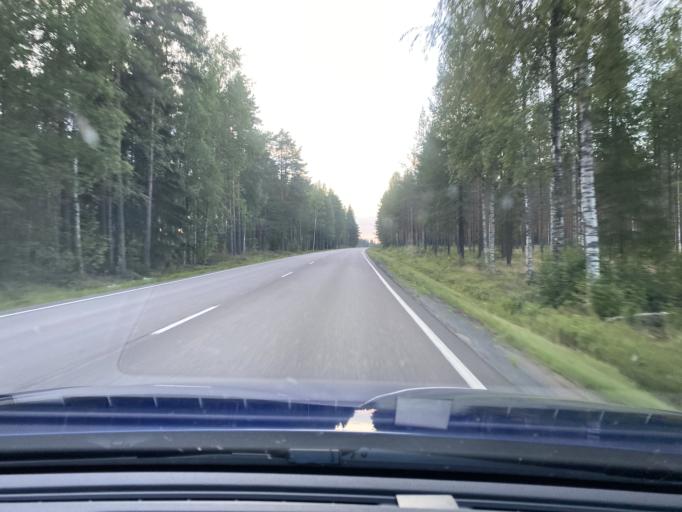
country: FI
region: Satakunta
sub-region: Pohjois-Satakunta
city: Honkajoki
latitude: 61.9077
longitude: 22.2685
